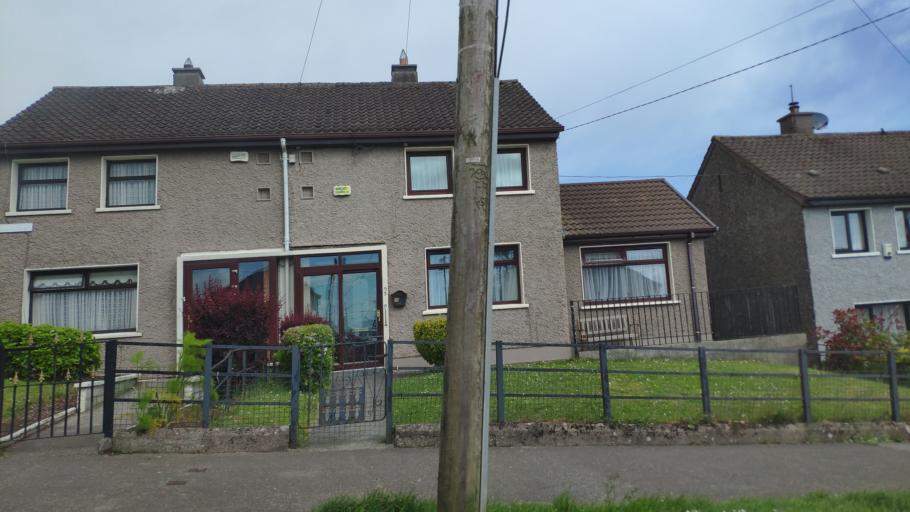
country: IE
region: Munster
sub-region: County Cork
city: Cork
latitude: 51.9134
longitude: -8.4882
